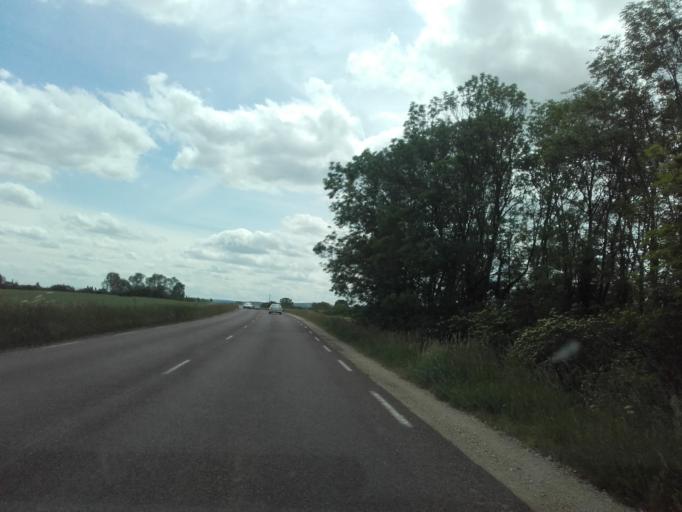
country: FR
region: Bourgogne
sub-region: Departement de la Cote-d'Or
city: Meursault
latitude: 46.9591
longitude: 4.7683
